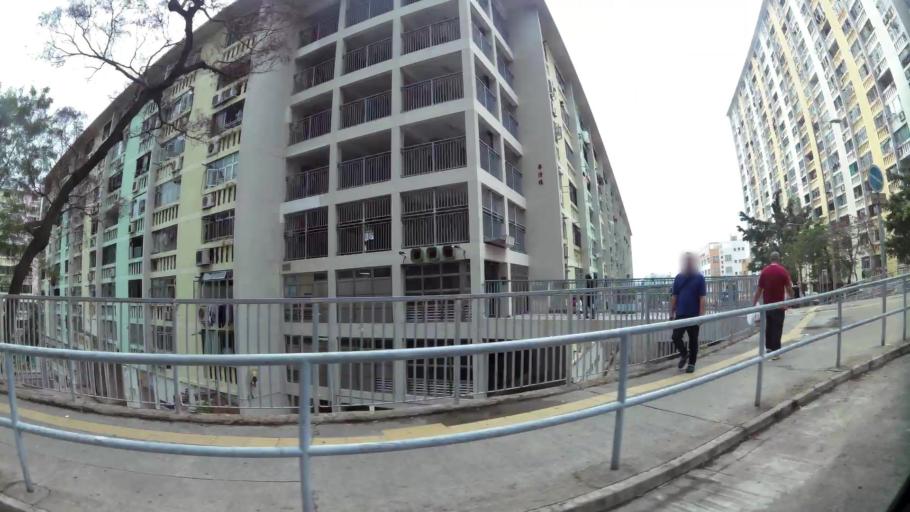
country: HK
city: Yung Shue Wan
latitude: 22.2521
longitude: 114.1360
